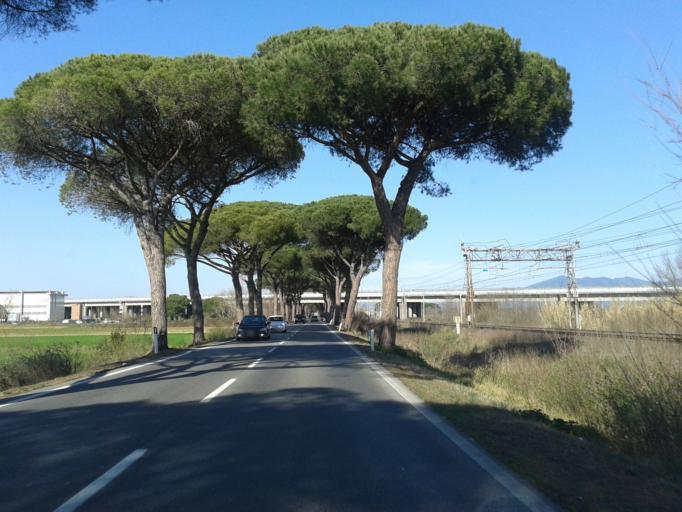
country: IT
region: Tuscany
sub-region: Province of Pisa
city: Pisa
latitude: 43.6579
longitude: 10.3672
